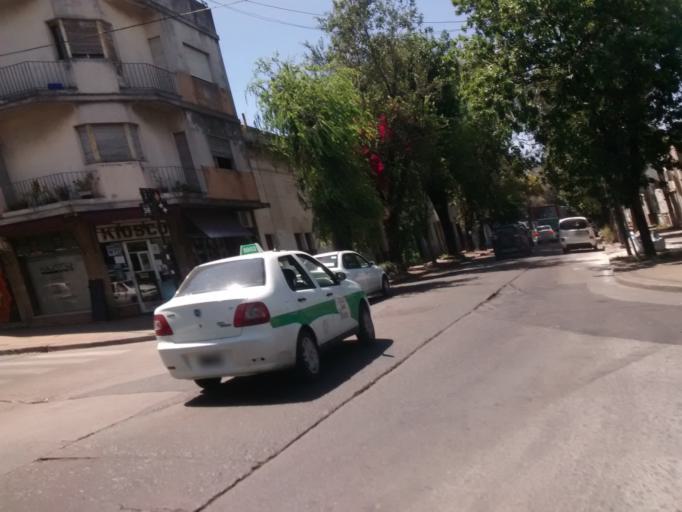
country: AR
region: Buenos Aires
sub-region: Partido de La Plata
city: La Plata
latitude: -34.9010
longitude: -57.9570
